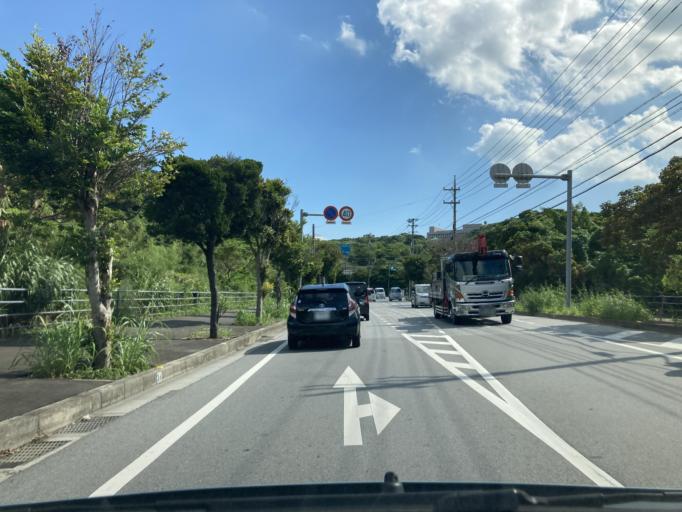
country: JP
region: Okinawa
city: Ginowan
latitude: 26.2478
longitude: 127.7577
